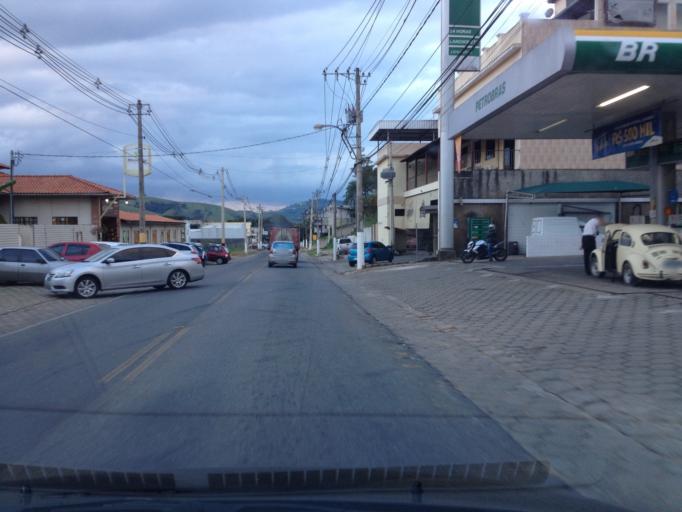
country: BR
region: Minas Gerais
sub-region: Sao Lourenco
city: Sao Lourenco
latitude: -22.1038
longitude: -45.0528
